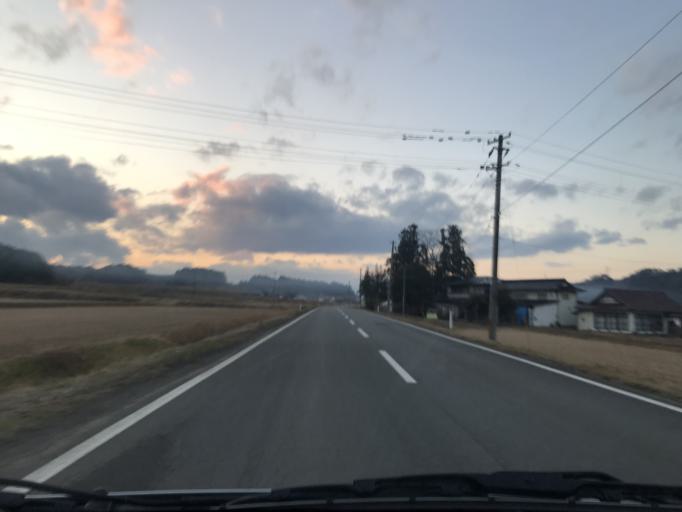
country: JP
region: Iwate
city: Ichinoseki
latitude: 38.8414
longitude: 141.1250
